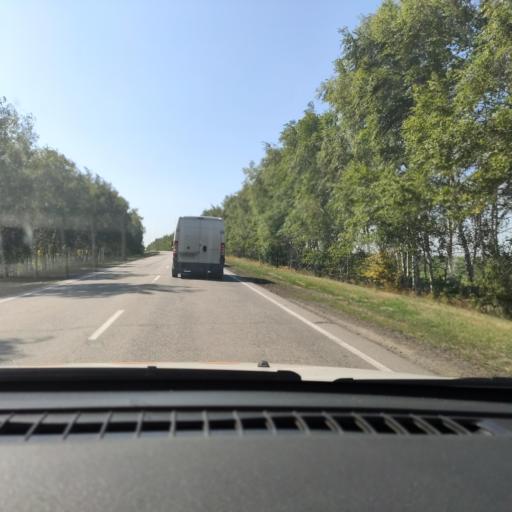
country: RU
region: Voronezj
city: Liski
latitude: 50.7965
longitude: 39.3633
